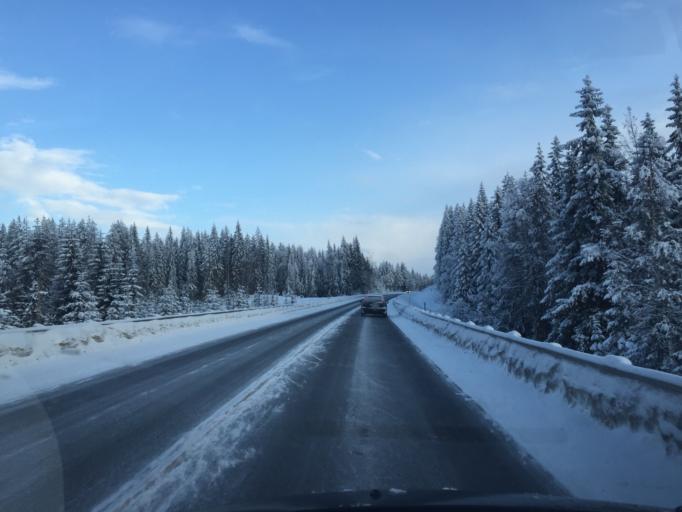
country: NO
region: Hedmark
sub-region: Trysil
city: Innbygda
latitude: 61.1018
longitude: 12.0077
